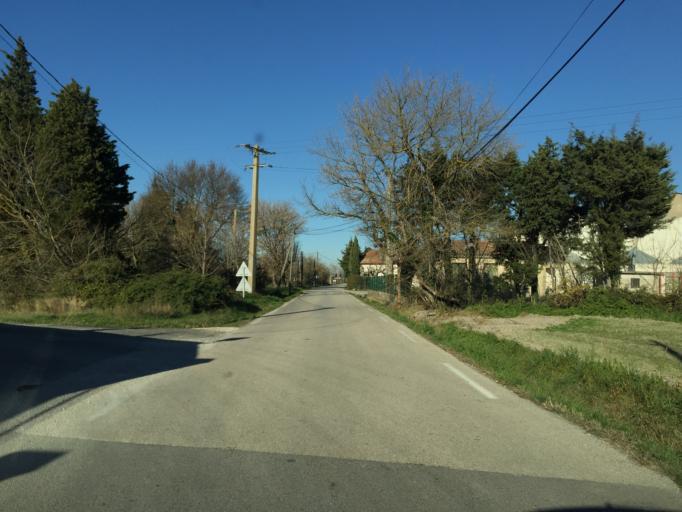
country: FR
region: Provence-Alpes-Cote d'Azur
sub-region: Departement du Vaucluse
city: Entraigues-sur-la-Sorgue
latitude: 44.0148
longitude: 4.9326
